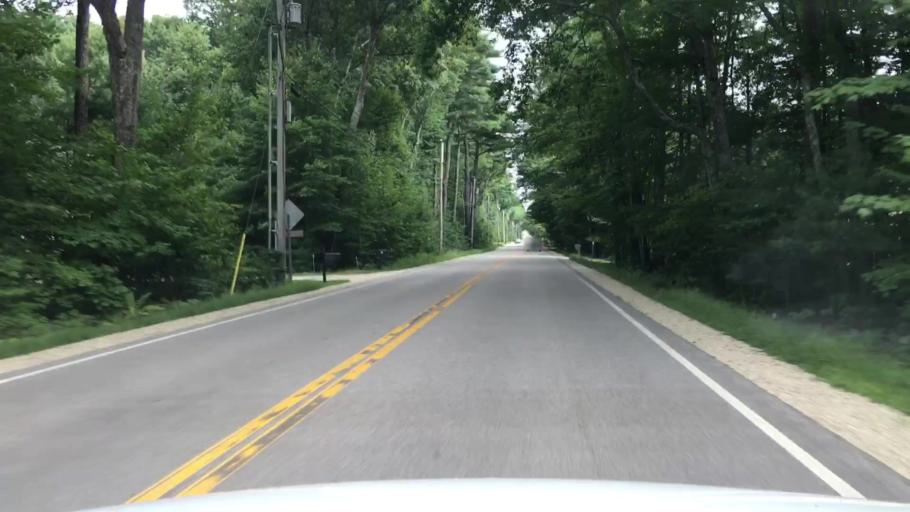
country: US
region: New Hampshire
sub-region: Strafford County
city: Somersworth
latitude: 43.2440
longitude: -70.9099
